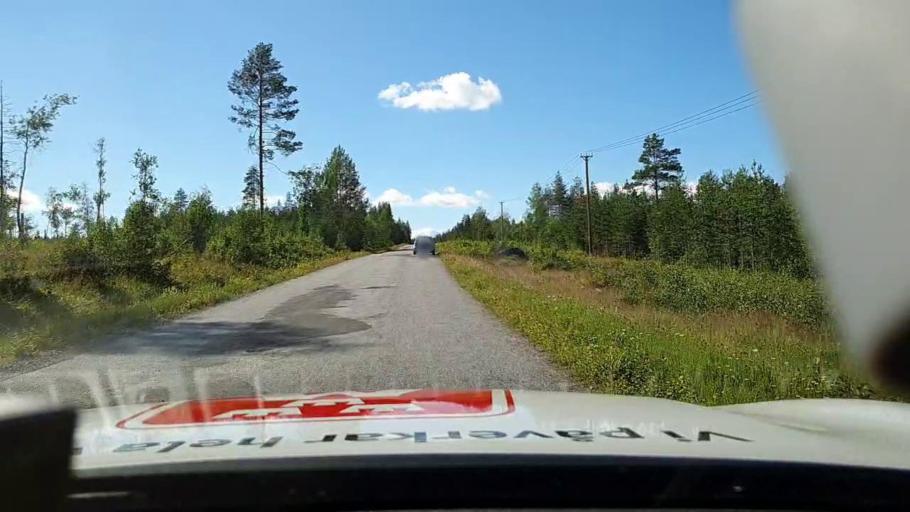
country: SE
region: Norrbotten
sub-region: Overkalix Kommun
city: OEverkalix
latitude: 66.2580
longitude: 23.0651
